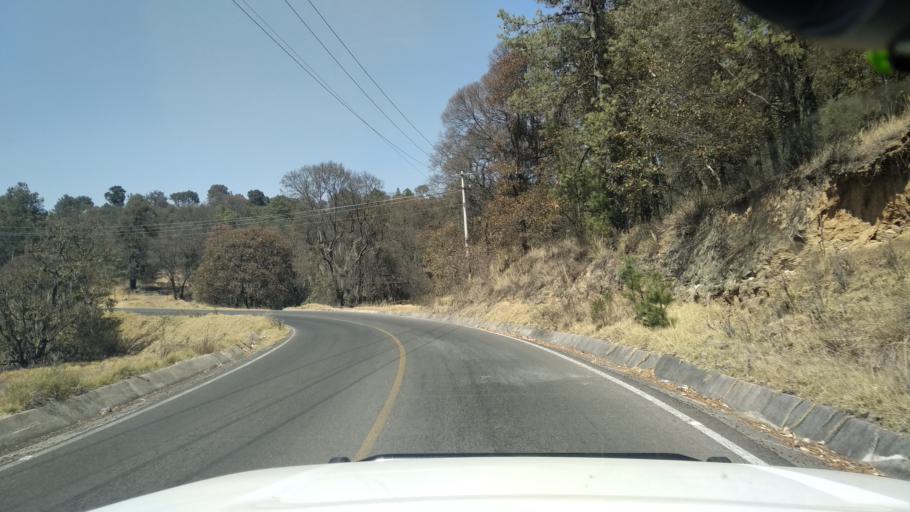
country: MX
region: Tlaxcala
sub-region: Nanacamilpa de Mariano Arista
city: Ciudad de Nanacamilpa
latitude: 19.4659
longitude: -98.5103
